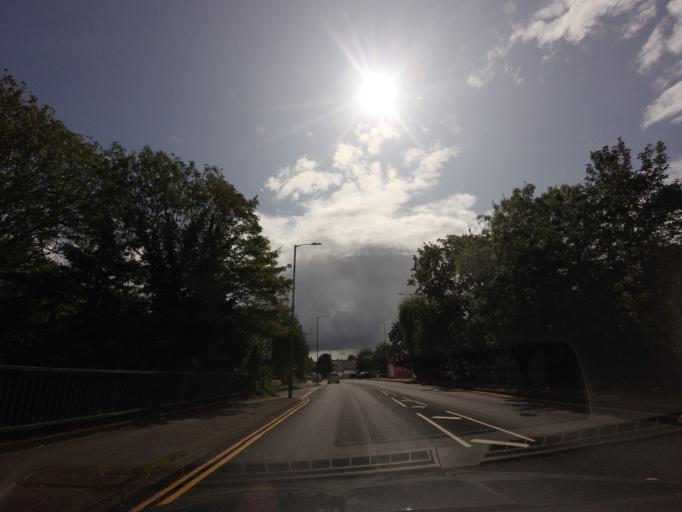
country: GB
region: England
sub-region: Kent
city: Tonbridge
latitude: 51.1955
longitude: 0.2843
